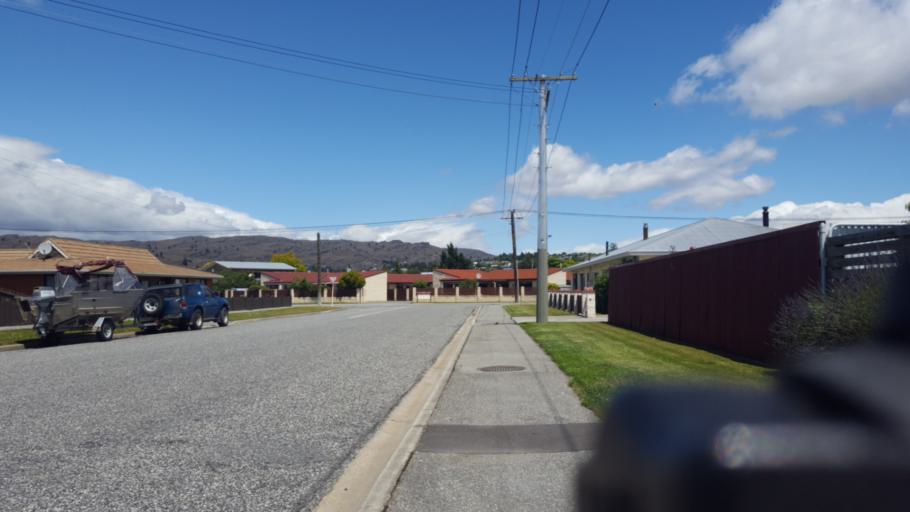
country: NZ
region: Otago
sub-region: Queenstown-Lakes District
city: Wanaka
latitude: -45.2474
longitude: 169.3864
